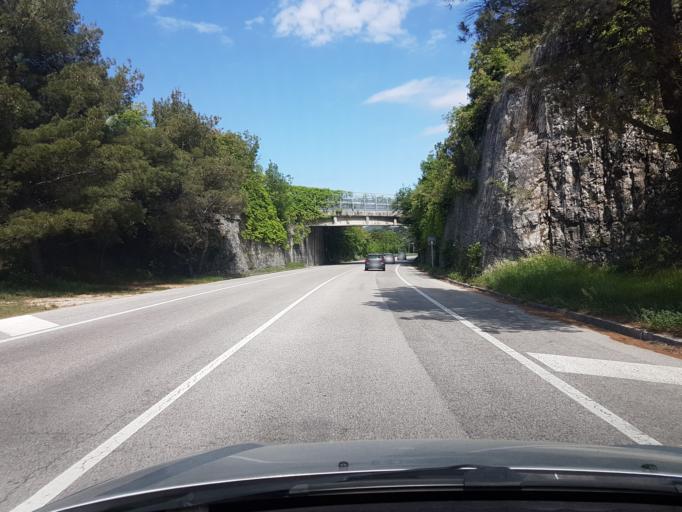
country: IT
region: Friuli Venezia Giulia
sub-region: Provincia di Trieste
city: Sistiana-Visogliano
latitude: 45.7614
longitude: 13.6399
